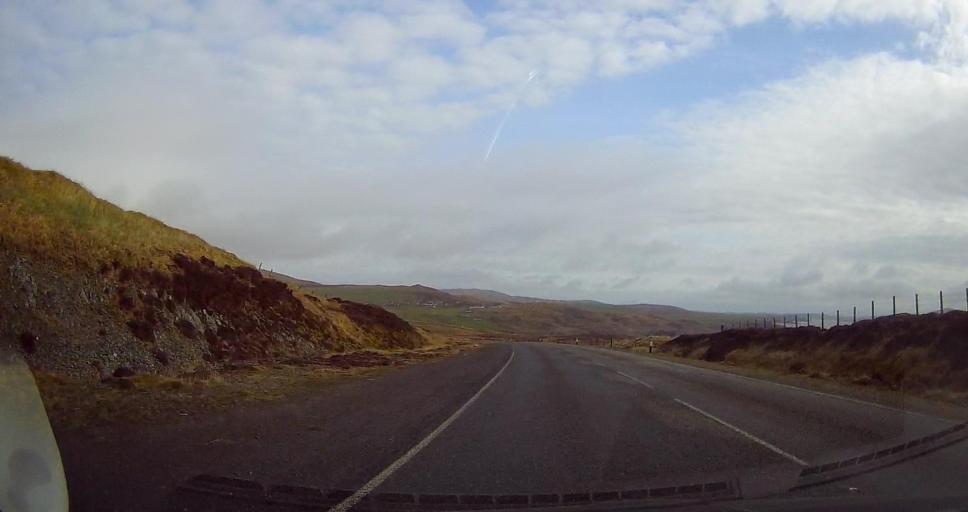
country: GB
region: Scotland
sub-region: Shetland Islands
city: Sandwick
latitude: 60.0890
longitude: -1.2292
